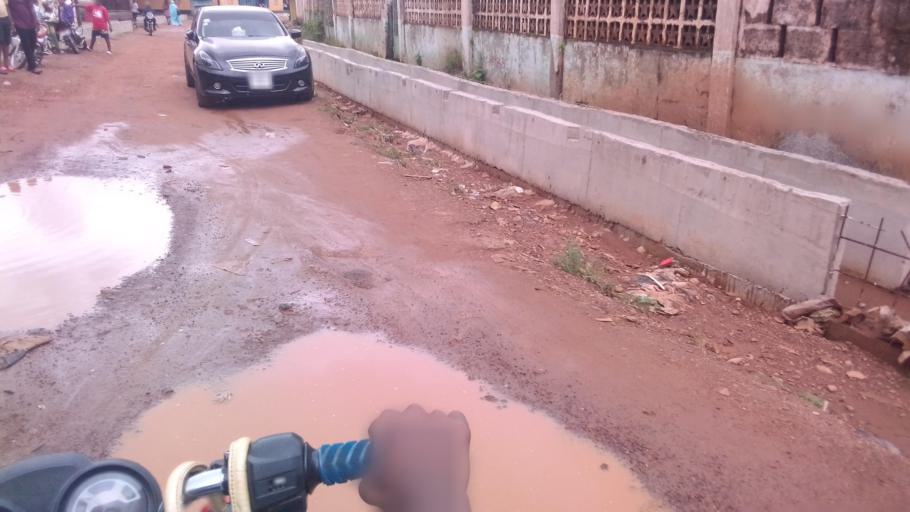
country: SL
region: Eastern Province
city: Kenema
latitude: 7.8856
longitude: -11.1847
